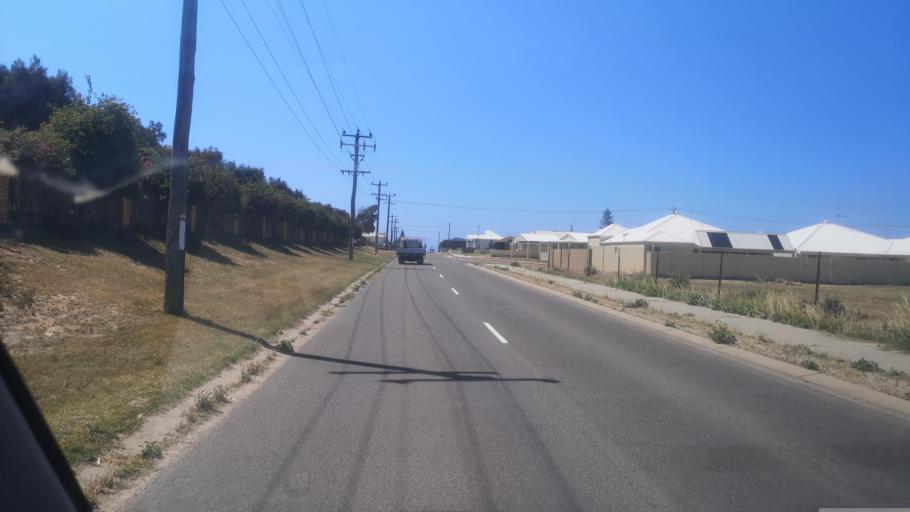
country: AU
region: Western Australia
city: Port Denison
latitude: -29.2791
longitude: 114.9193
